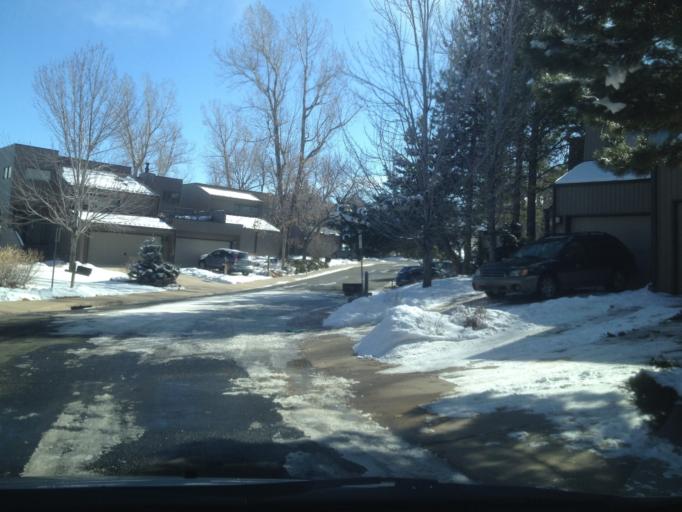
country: US
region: Colorado
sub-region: Boulder County
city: Boulder
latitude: 40.0473
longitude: -105.2909
